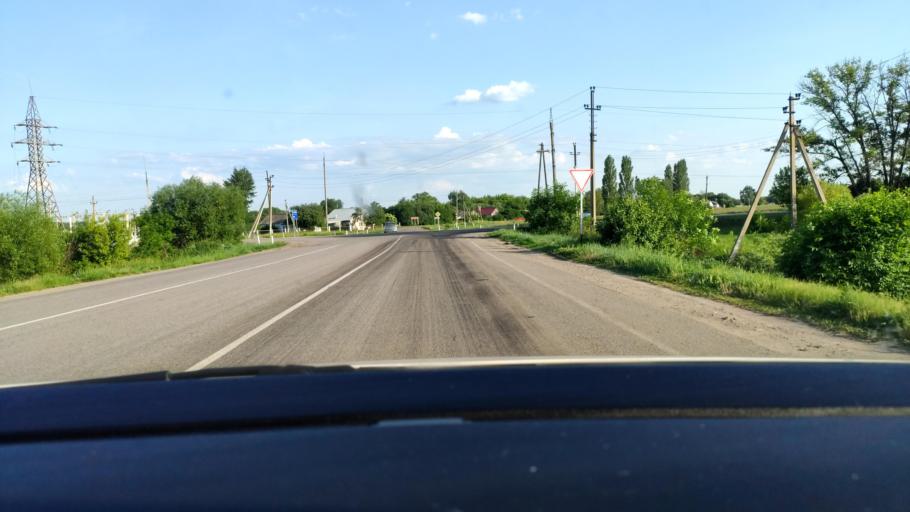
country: RU
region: Voronezj
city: Kashirskoye
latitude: 51.4677
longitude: 39.8632
